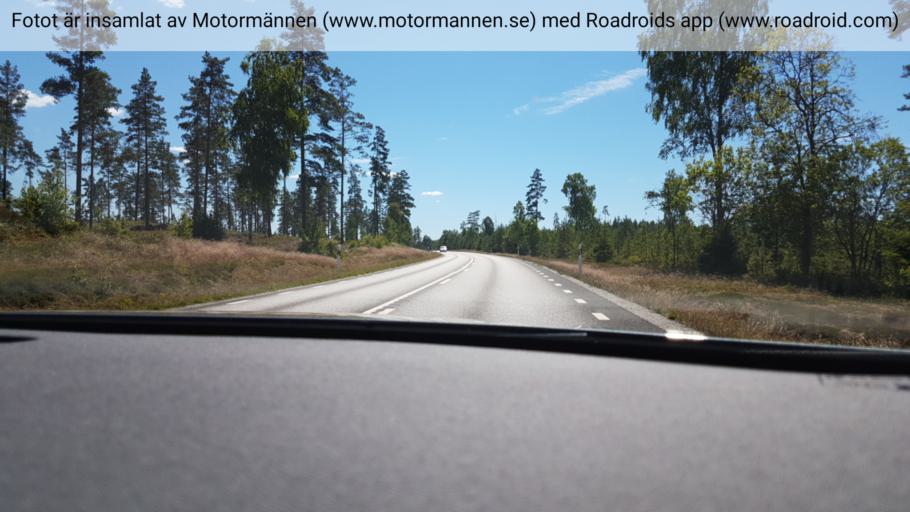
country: SE
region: Joenkoeping
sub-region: Gnosjo Kommun
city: Gnosjoe
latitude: 57.5310
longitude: 13.6859
